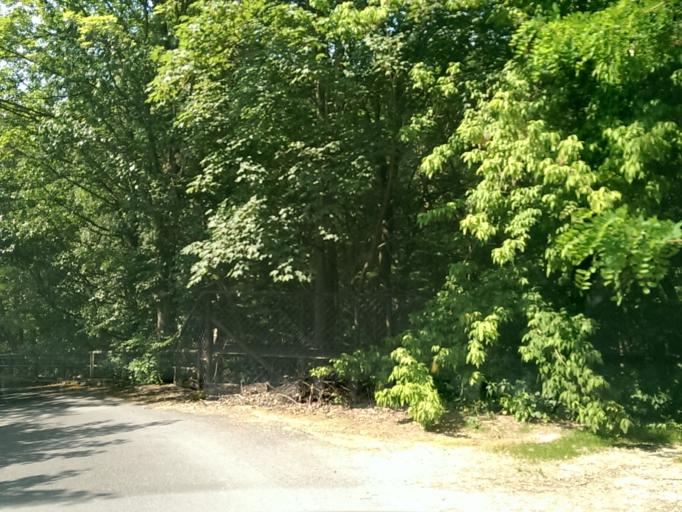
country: CZ
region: Kralovehradecky
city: Dvur Kralove nad Labem
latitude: 50.4337
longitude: 15.7860
